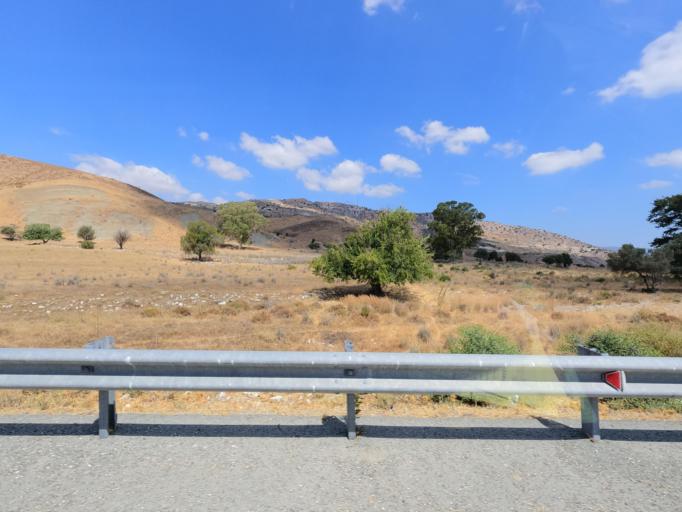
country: CY
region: Limassol
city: Pachna
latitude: 34.8137
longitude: 32.7156
